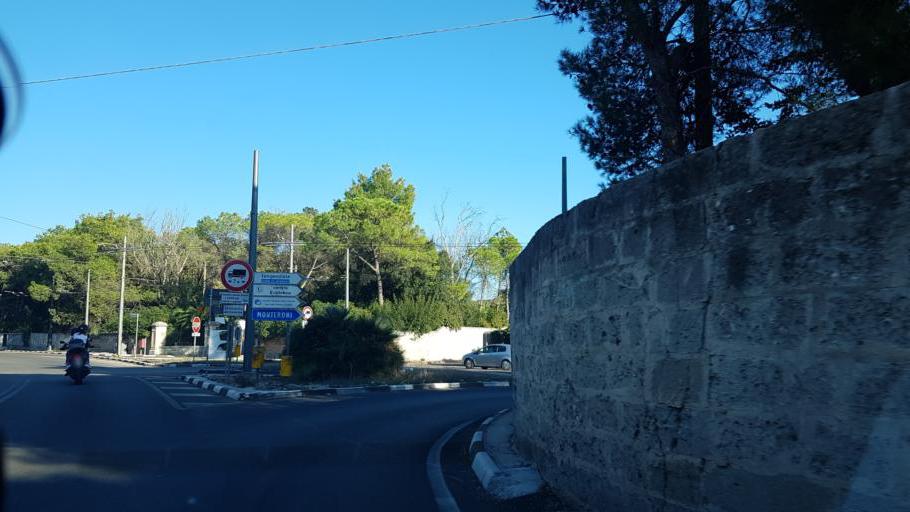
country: IT
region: Apulia
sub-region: Provincia di Lecce
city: San Pietro in Lama
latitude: 40.3400
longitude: 18.1353
